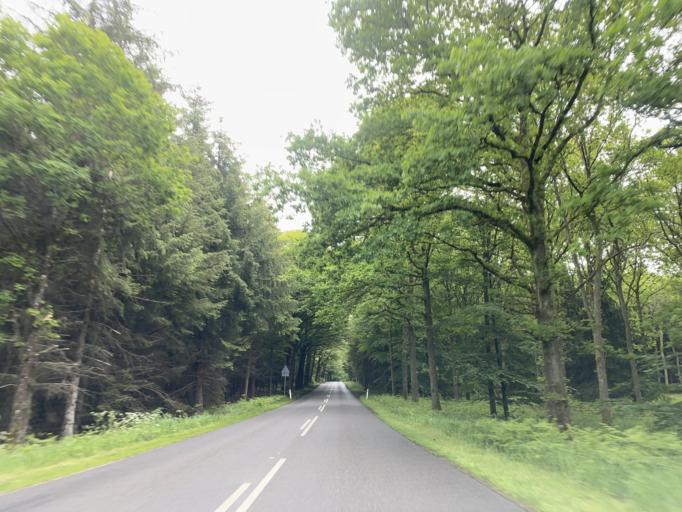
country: DK
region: Central Jutland
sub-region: Favrskov Kommune
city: Hammel
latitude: 56.2599
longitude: 9.9414
